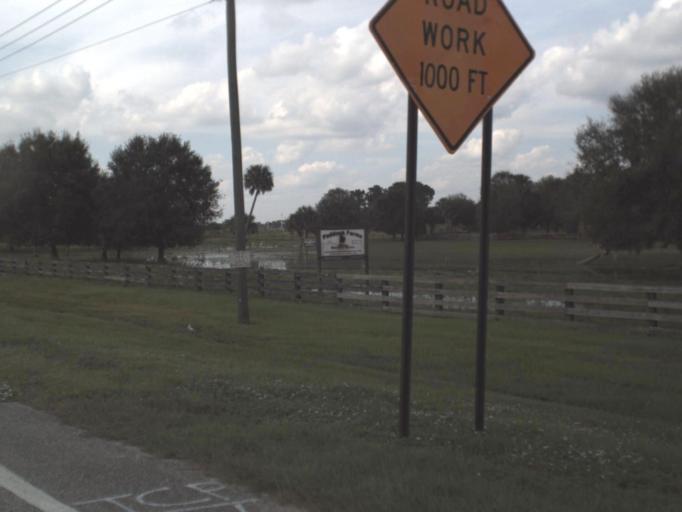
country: US
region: Florida
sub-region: Okeechobee County
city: Taylor Creek
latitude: 27.2388
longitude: -80.7840
